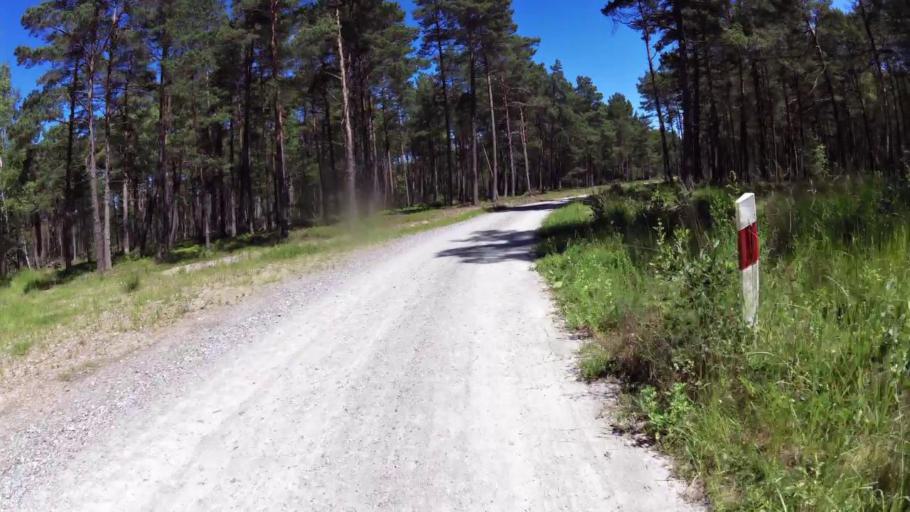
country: PL
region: West Pomeranian Voivodeship
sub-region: Powiat gryficki
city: Trzebiatow
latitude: 54.1023
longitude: 15.1707
